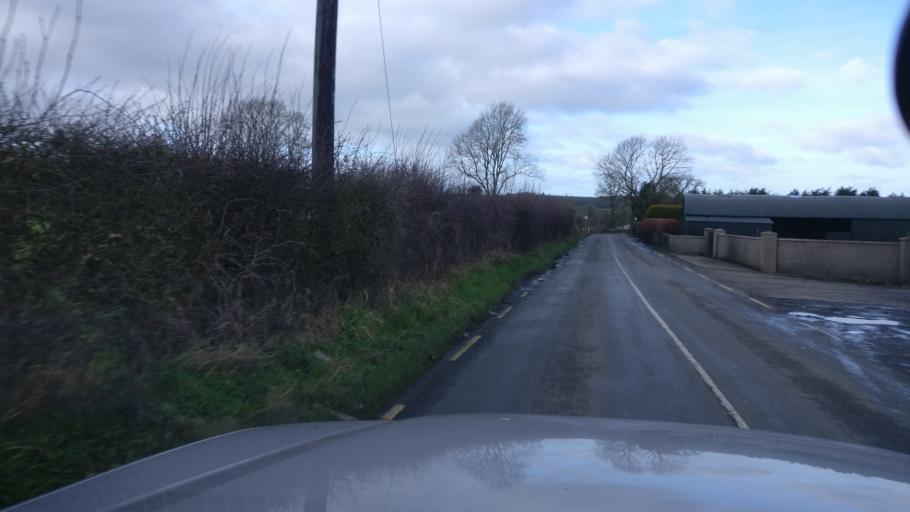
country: IE
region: Leinster
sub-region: Kilkenny
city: Castlecomer
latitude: 52.8125
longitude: -7.2119
